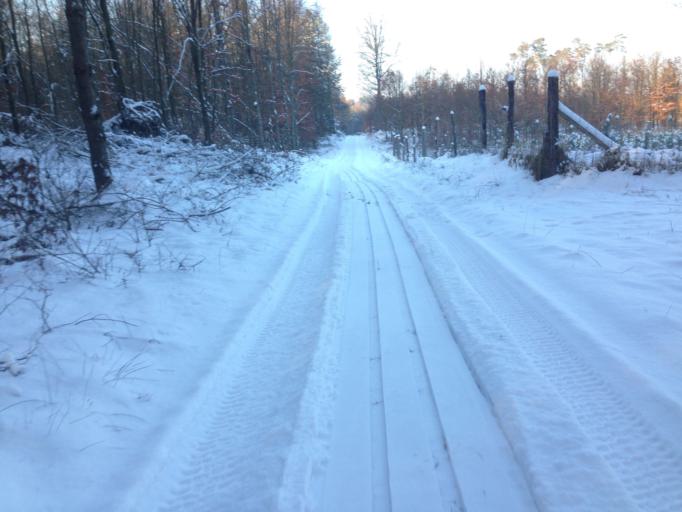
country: PL
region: Kujawsko-Pomorskie
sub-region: Powiat brodnicki
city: Gorzno
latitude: 53.1821
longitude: 19.6838
